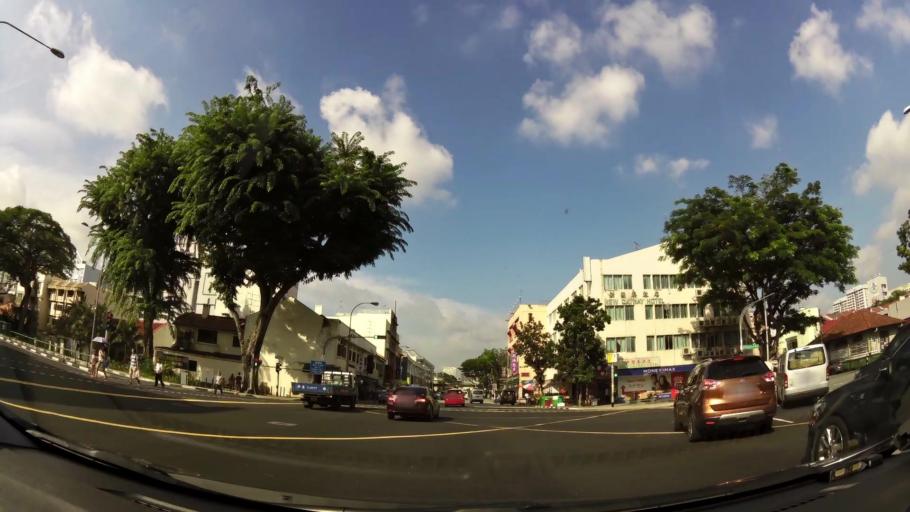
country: SG
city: Singapore
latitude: 1.3131
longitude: 103.8823
